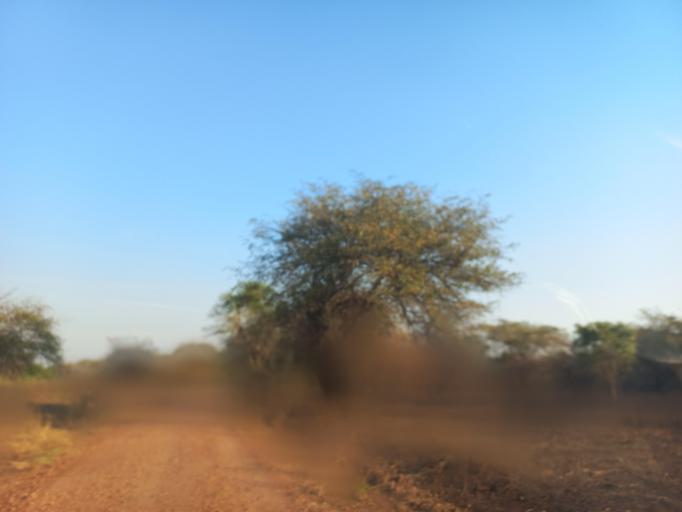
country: ZM
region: Lusaka
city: Luangwa
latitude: -15.4315
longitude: 30.3428
